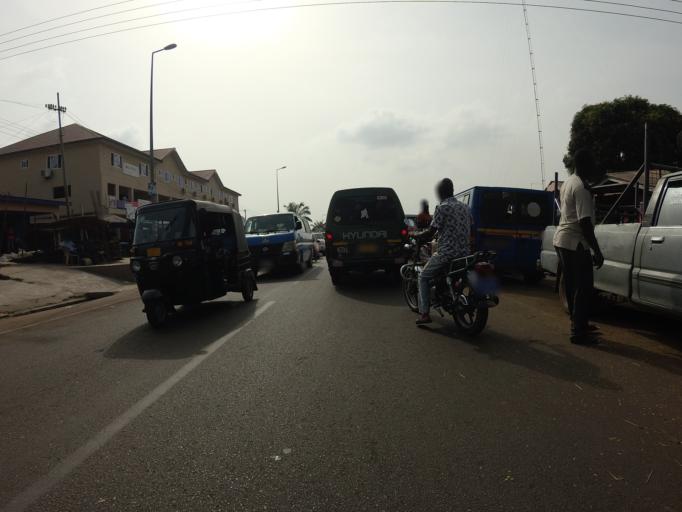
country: GH
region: Volta
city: Ho
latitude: 6.6168
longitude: 0.4728
